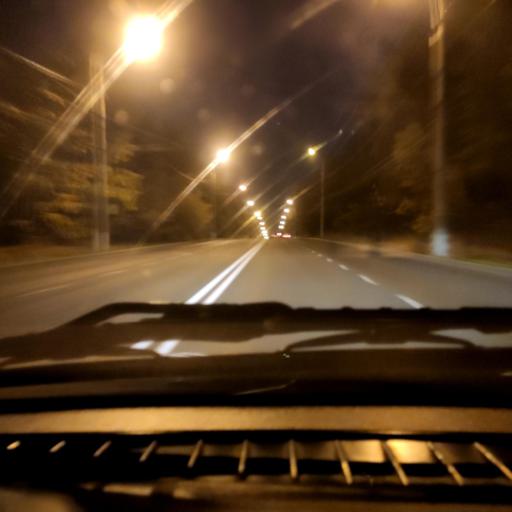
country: RU
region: Samara
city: Zhigulevsk
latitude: 53.4961
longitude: 49.4630
